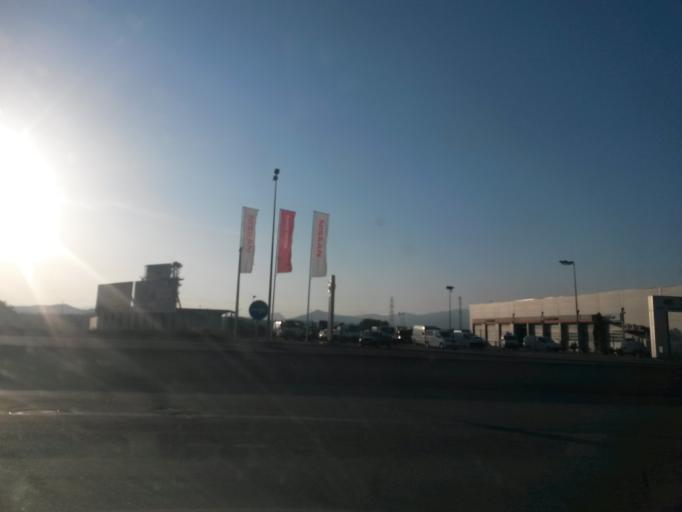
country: ES
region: Catalonia
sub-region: Provincia de Girona
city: Fornells de la Selva
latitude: 41.9336
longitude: 2.7966
